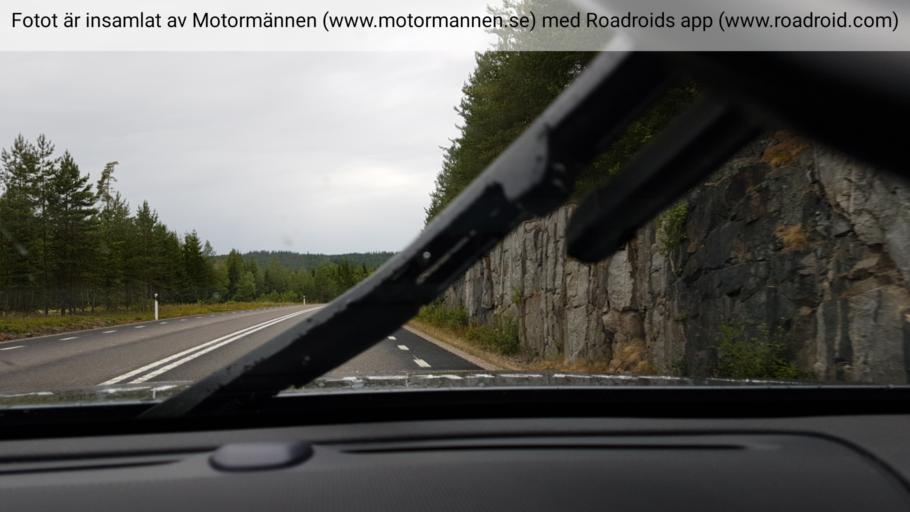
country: SE
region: Dalarna
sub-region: Faluns Kommun
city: Bjursas
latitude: 60.7881
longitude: 15.2836
